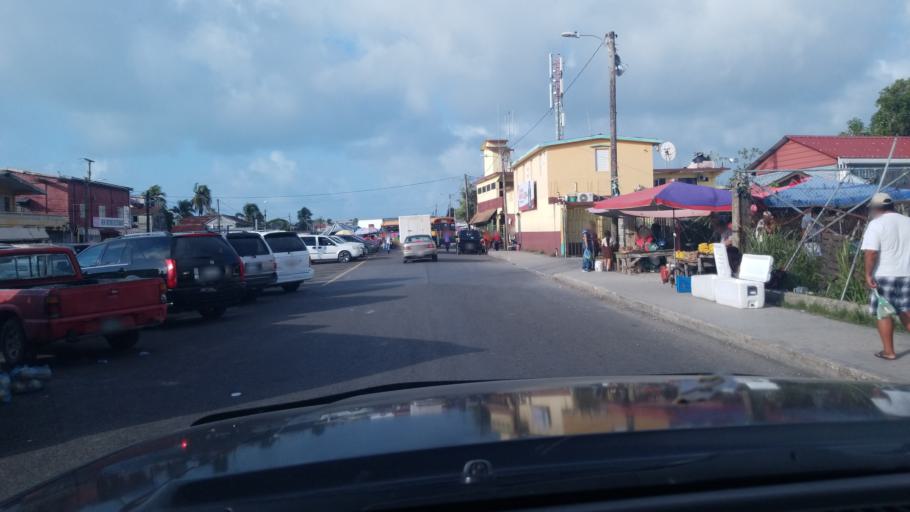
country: BZ
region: Belize
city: Belize City
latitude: 17.4948
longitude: -88.1927
